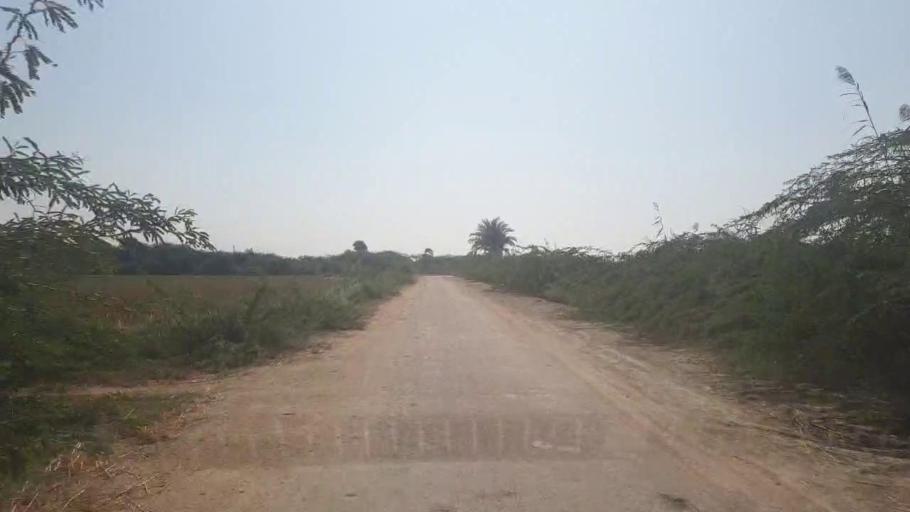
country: PK
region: Sindh
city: Badin
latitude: 24.6478
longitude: 68.9168
